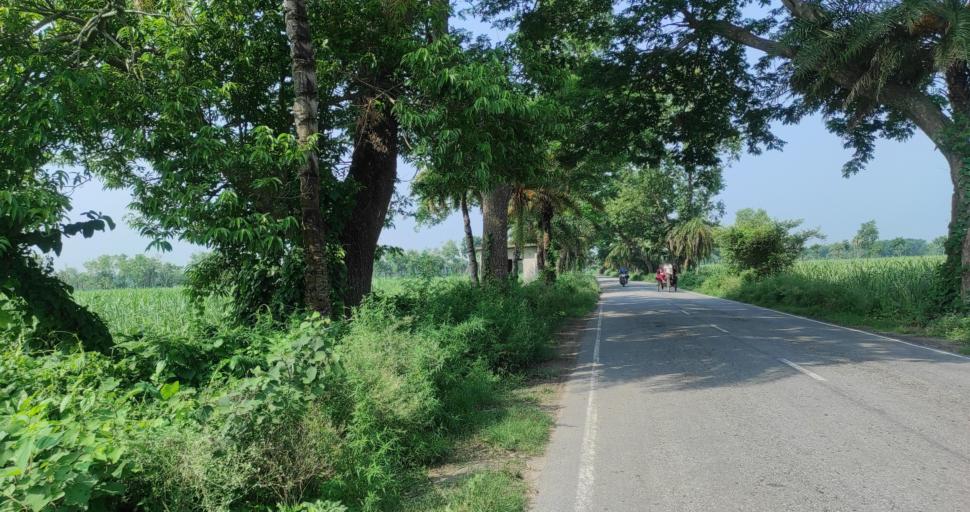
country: BD
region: Rajshahi
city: Ishurdi
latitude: 24.2677
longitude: 89.0525
